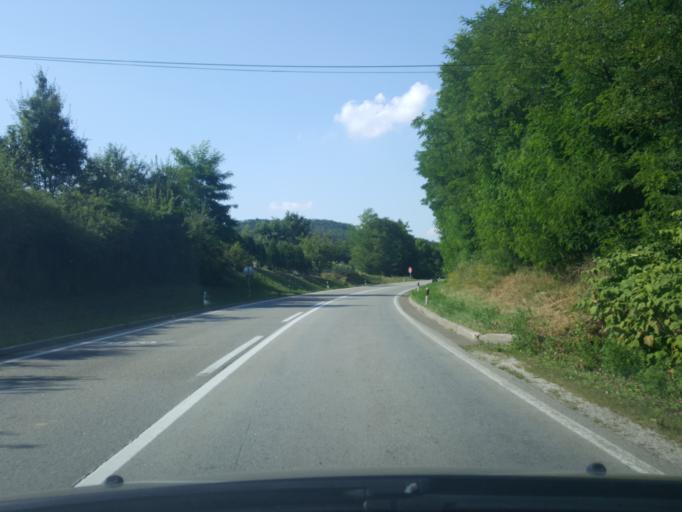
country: RS
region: Central Serbia
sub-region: Moravicki Okrug
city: Gornji Milanovac
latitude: 44.0885
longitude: 20.4792
